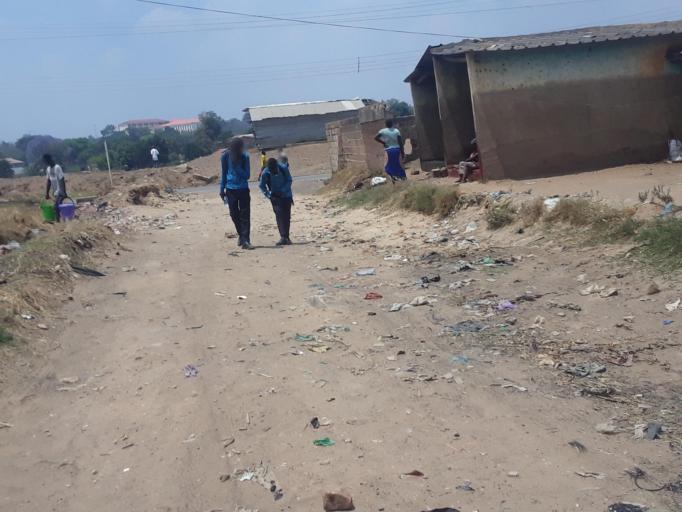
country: ZM
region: Lusaka
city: Lusaka
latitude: -15.3672
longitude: 28.2982
